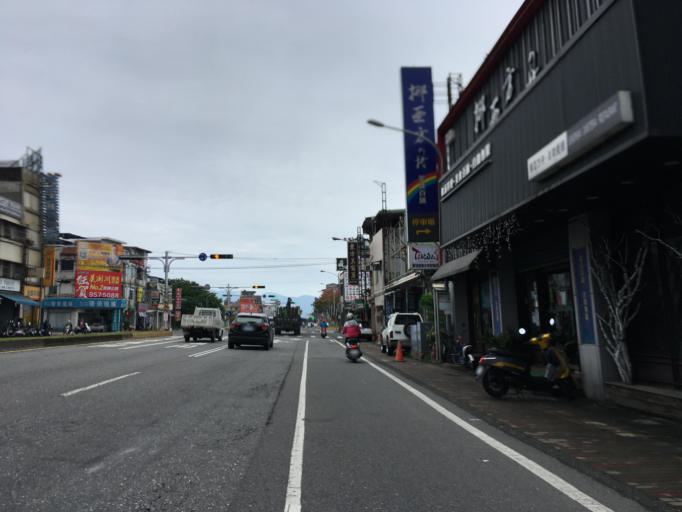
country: TW
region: Taiwan
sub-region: Yilan
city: Yilan
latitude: 24.6924
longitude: 121.7698
